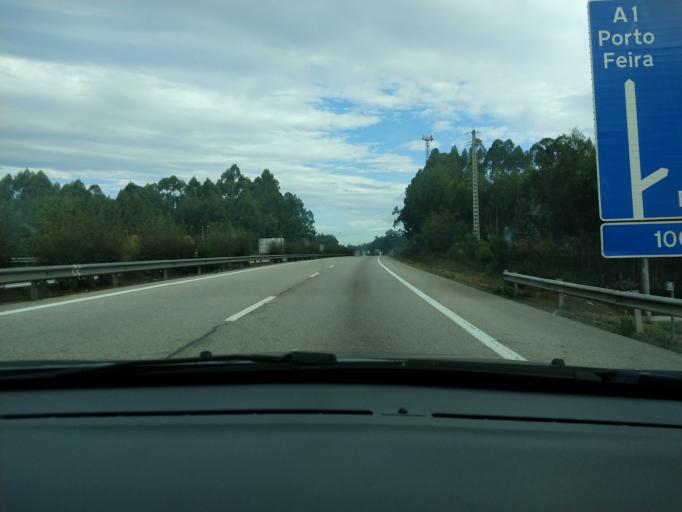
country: PT
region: Aveiro
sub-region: Estarreja
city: Beduido
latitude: 40.7695
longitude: -8.5436
